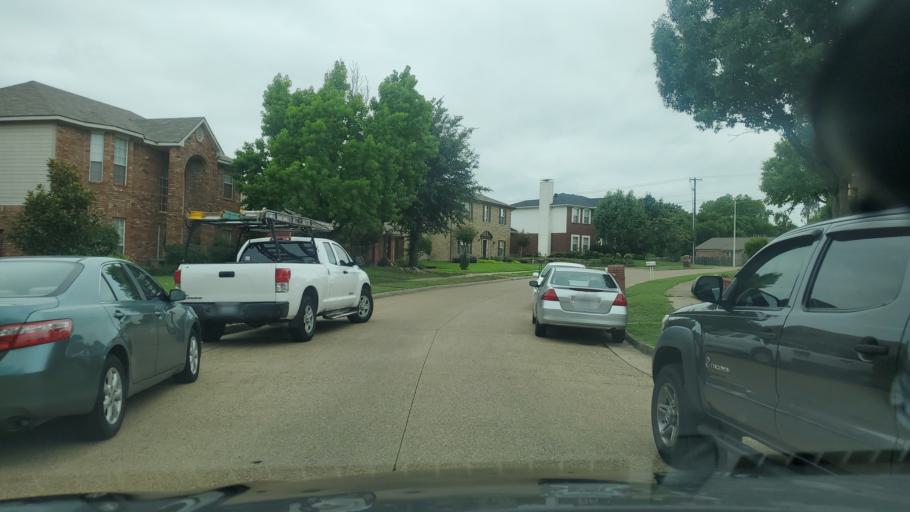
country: US
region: Texas
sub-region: Dallas County
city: Garland
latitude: 32.9531
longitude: -96.6644
